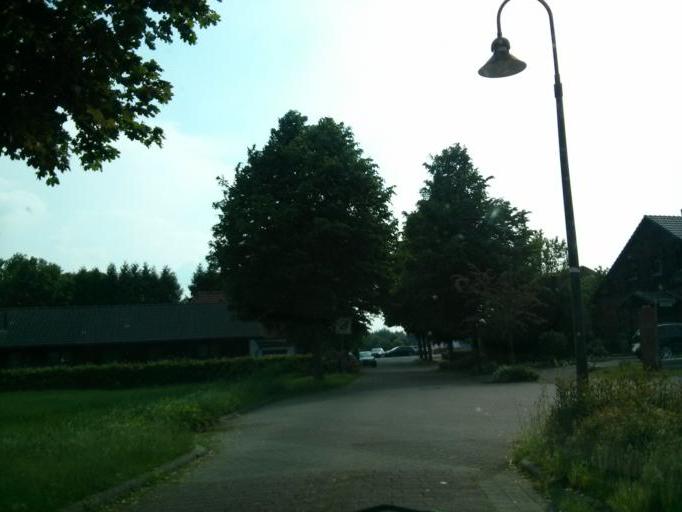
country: DE
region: Lower Saxony
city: Loxstedt
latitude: 53.4824
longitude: 8.6896
